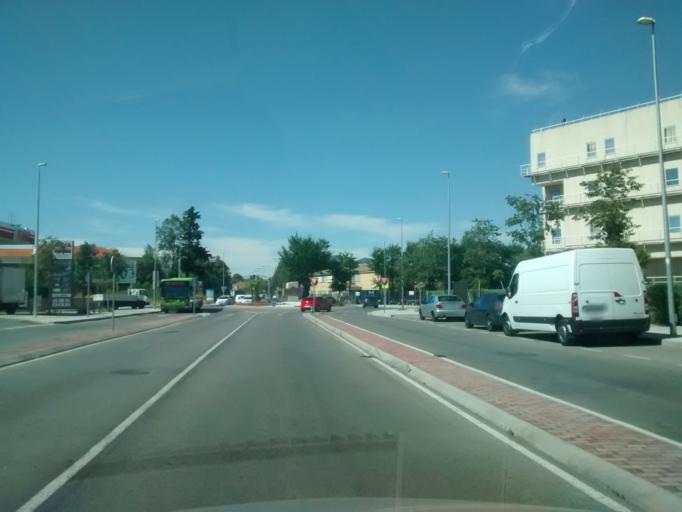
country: ES
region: Madrid
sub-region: Provincia de Madrid
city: San Fernando de Henares
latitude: 40.4361
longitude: -3.5326
